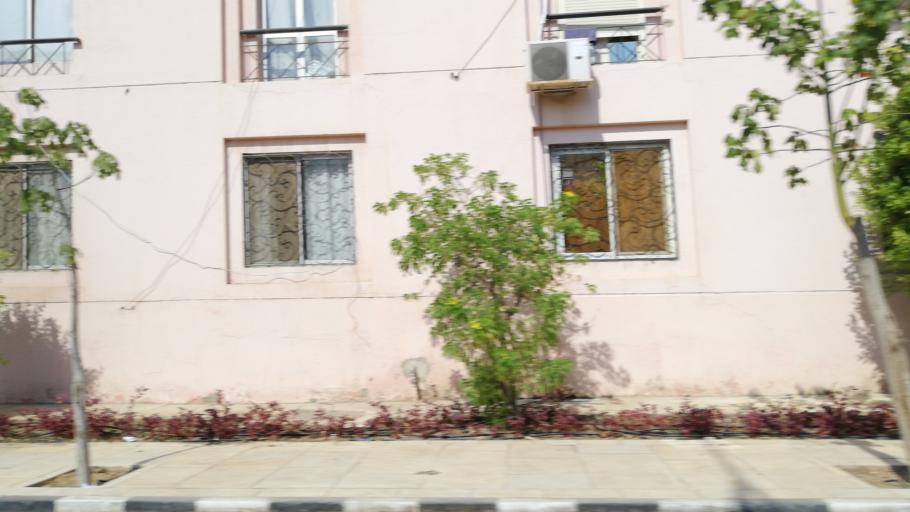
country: EG
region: Muhafazat al Qalyubiyah
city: Al Khankah
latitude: 30.0632
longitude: 31.4872
